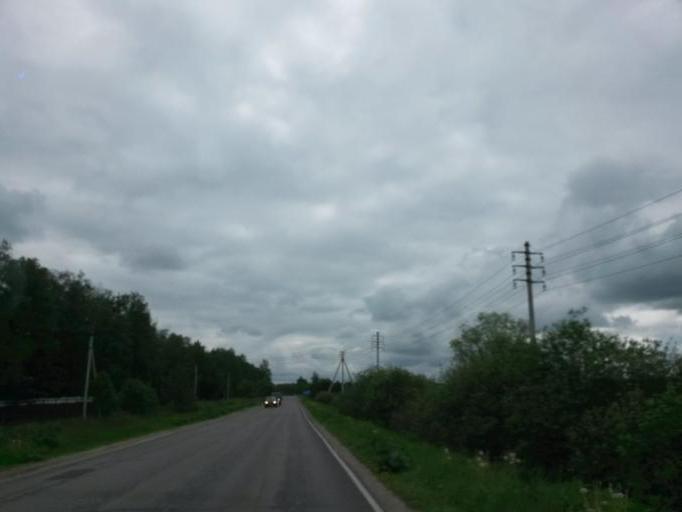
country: RU
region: Moskovskaya
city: L'vovskiy
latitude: 55.3246
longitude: 37.6118
